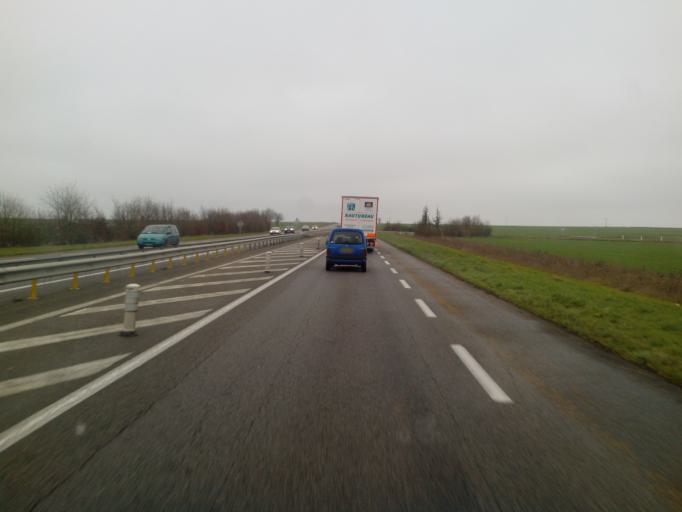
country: FR
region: Poitou-Charentes
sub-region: Departement de la Vienne
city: Vouille
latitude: 46.6516
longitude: 0.1332
